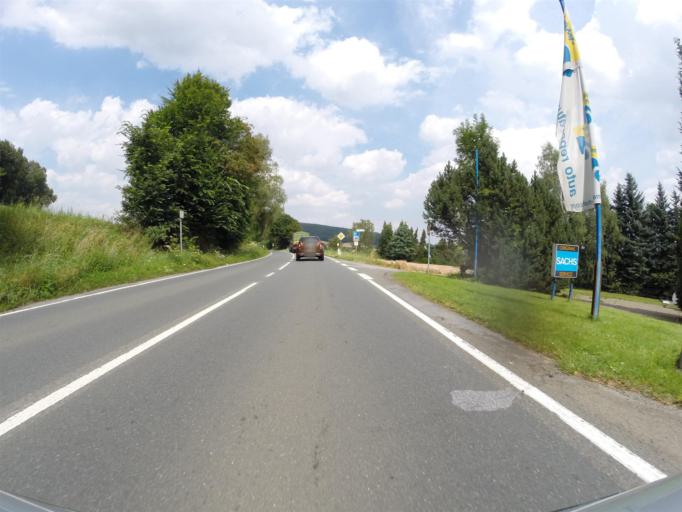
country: DE
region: North Rhine-Westphalia
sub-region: Regierungsbezirk Detmold
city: Rodinghausen
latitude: 52.2718
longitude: 8.5165
